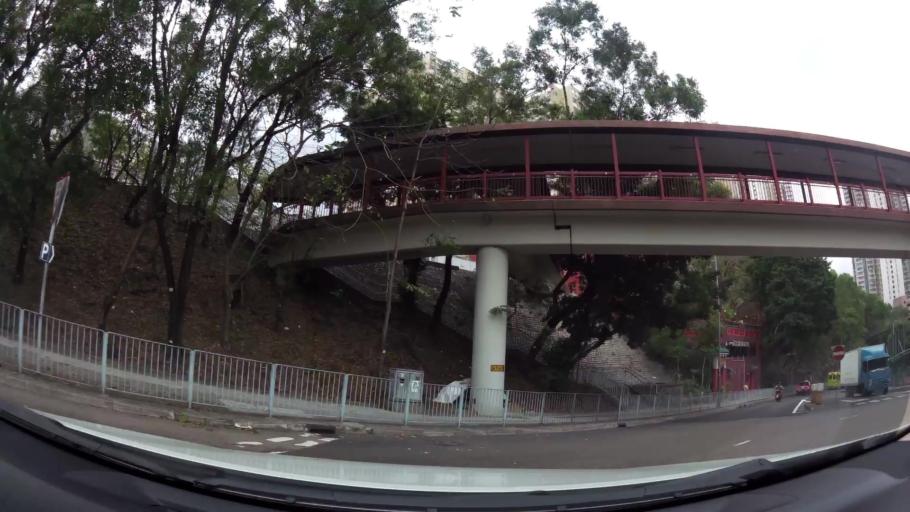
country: HK
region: Wong Tai Sin
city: Wong Tai Sin
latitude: 22.3434
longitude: 114.1892
